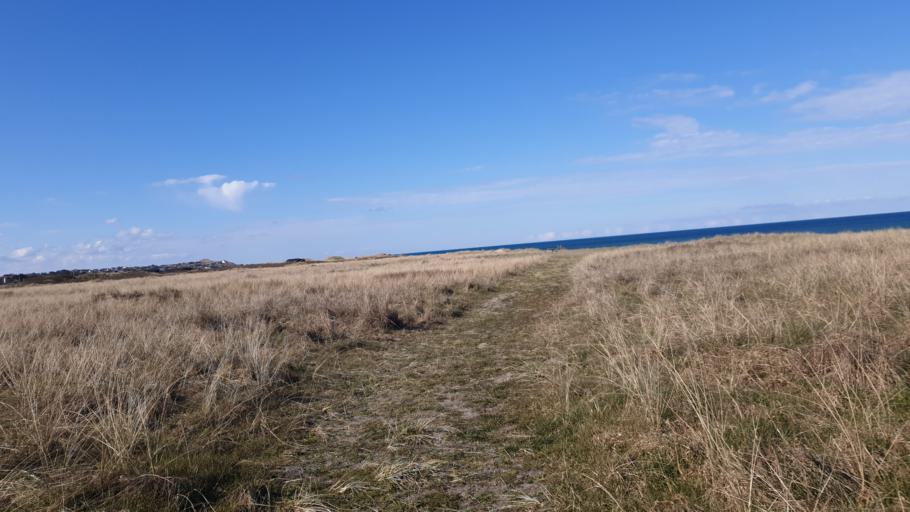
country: DK
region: North Denmark
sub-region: Hjorring Kommune
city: Hjorring
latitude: 57.4943
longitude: 9.8307
